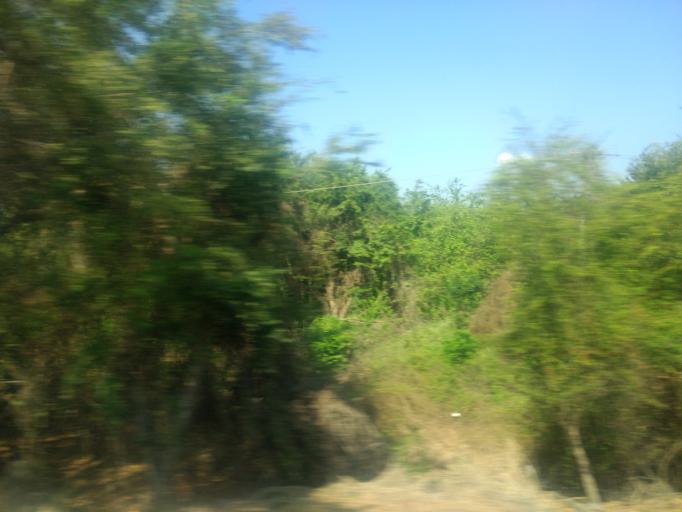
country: MX
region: Colima
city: El Colomo
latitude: 19.0432
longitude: -104.2602
